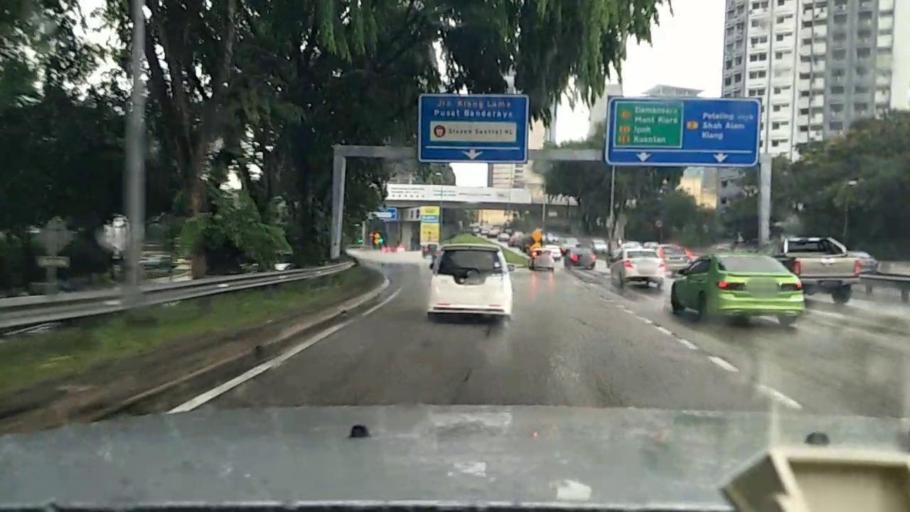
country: MY
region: Kuala Lumpur
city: Kuala Lumpur
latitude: 3.1138
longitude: 101.6804
